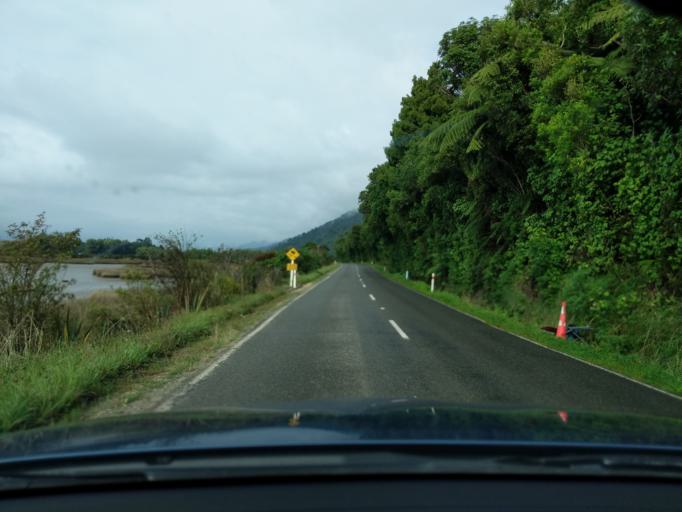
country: NZ
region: Tasman
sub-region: Tasman District
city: Takaka
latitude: -40.6525
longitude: 172.6535
